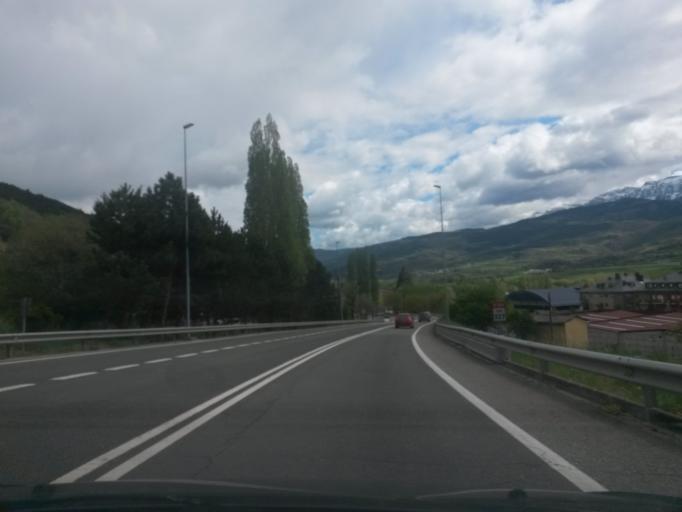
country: ES
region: Catalonia
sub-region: Provincia de Lleida
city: la Seu d'Urgell
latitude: 42.3620
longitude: 1.4631
